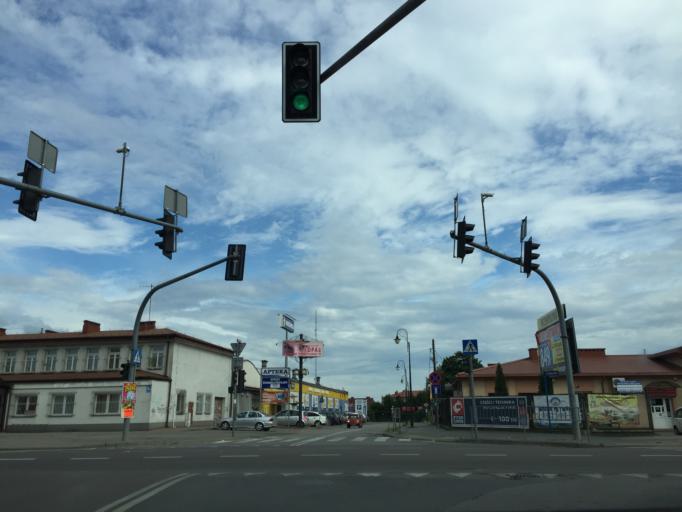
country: PL
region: Lublin Voivodeship
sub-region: Powiat lukowski
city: Lukow
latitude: 51.9326
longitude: 22.3858
